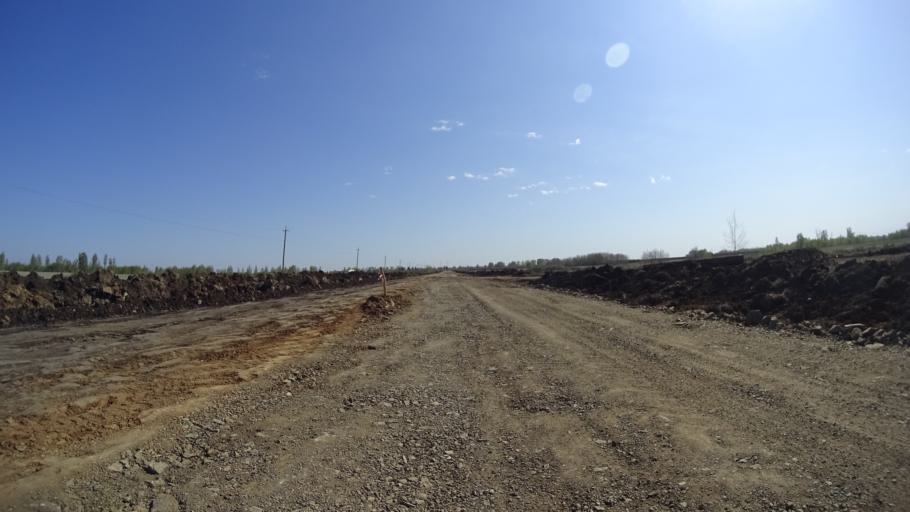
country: RU
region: Chelyabinsk
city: Troitsk
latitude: 54.1827
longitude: 61.4858
